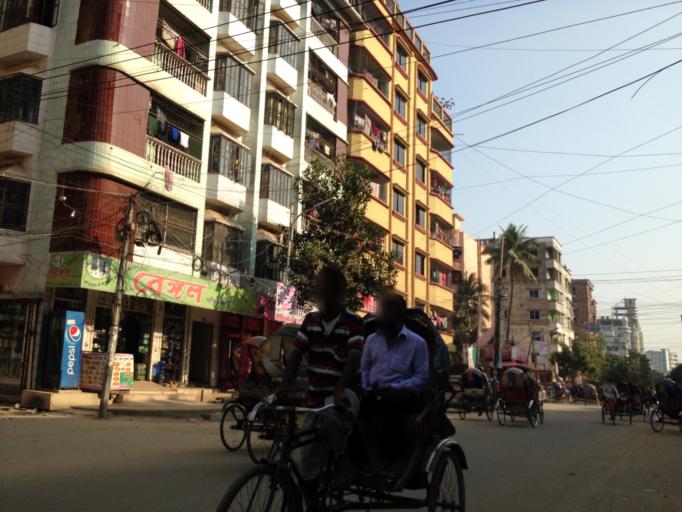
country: BD
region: Dhaka
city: Azimpur
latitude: 23.8012
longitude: 90.3498
